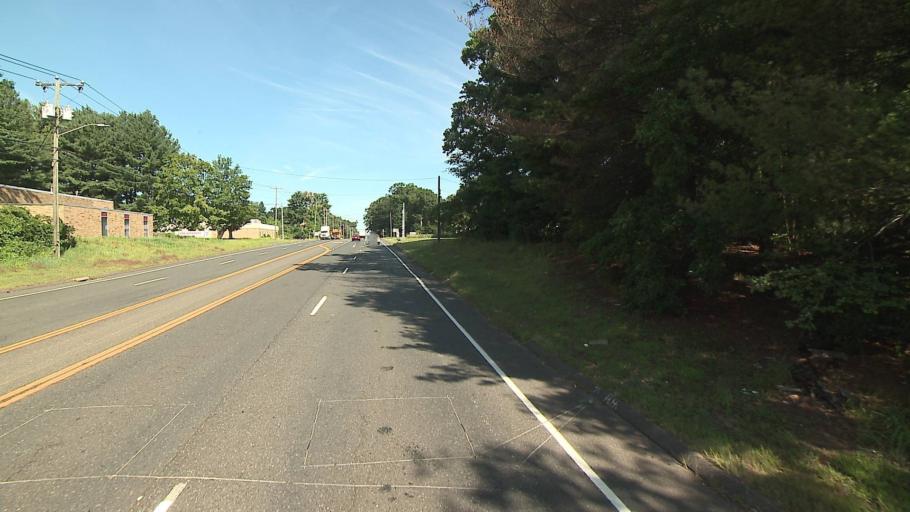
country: US
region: Connecticut
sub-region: Hartford County
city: Blue Hills
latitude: 41.8573
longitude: -72.7081
